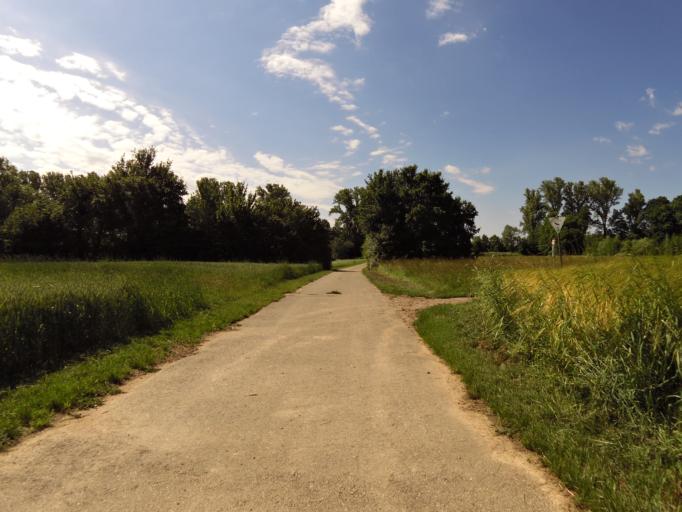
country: DE
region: Rheinland-Pfalz
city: Altdorf
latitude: 49.2833
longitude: 8.1987
